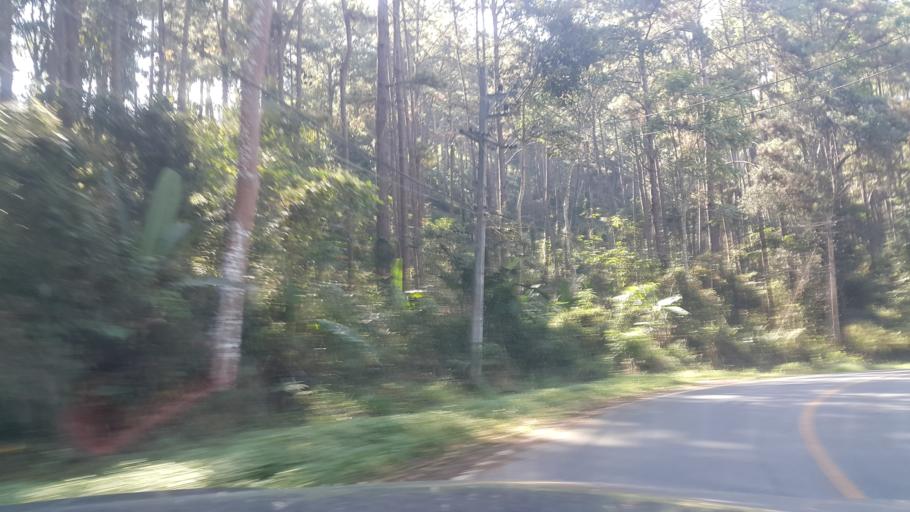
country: TH
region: Chiang Mai
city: Samoeng
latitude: 18.8755
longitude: 98.7953
